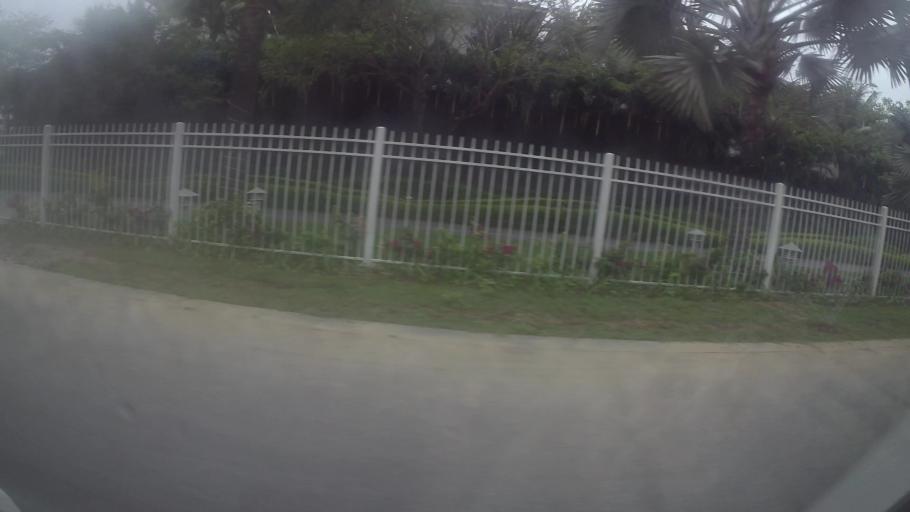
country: VN
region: Da Nang
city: Ngu Hanh Son
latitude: 16.0413
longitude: 108.2500
